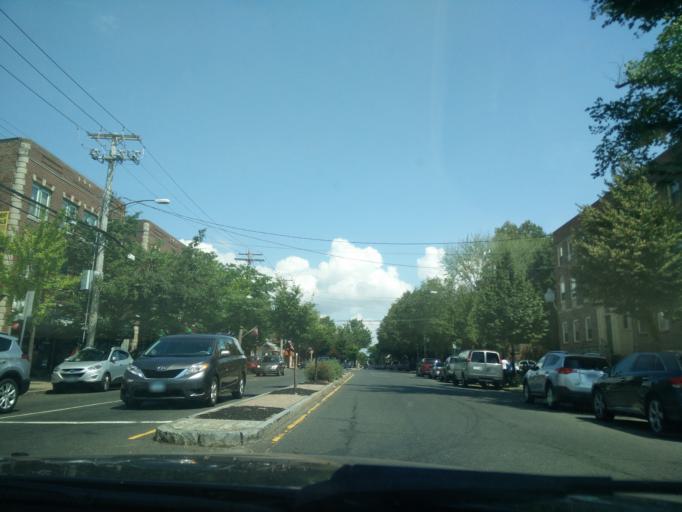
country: US
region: Connecticut
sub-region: Fairfield County
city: Bridgeport
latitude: 41.1575
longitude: -73.2264
